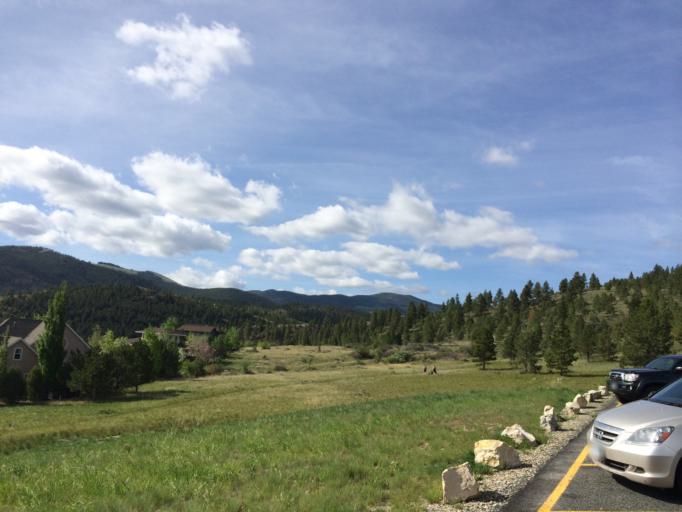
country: US
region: Montana
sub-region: Lewis and Clark County
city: Helena
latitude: 46.5876
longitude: -112.0494
